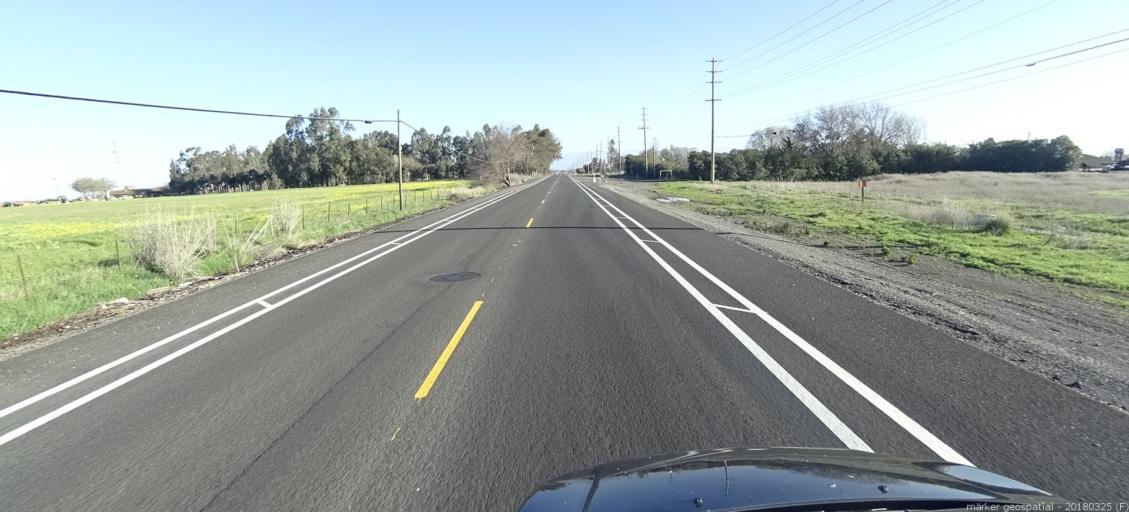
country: US
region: California
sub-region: Yolo County
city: West Sacramento
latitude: 38.6327
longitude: -121.5396
